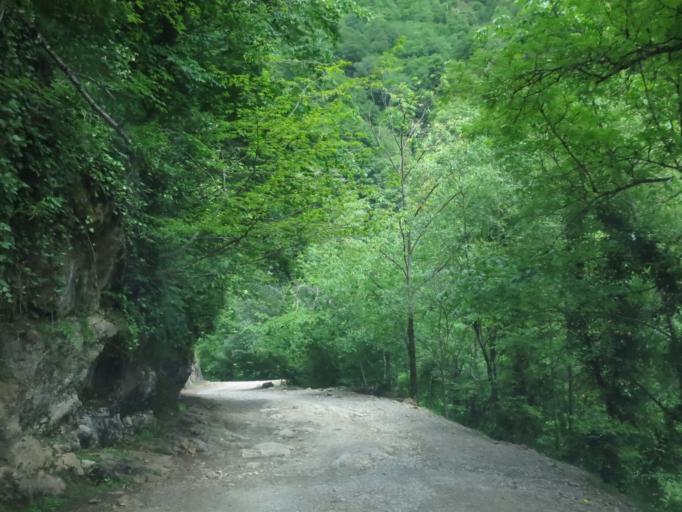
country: GE
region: Kakheti
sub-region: Telavi
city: Telavi
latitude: 42.2126
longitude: 45.4742
